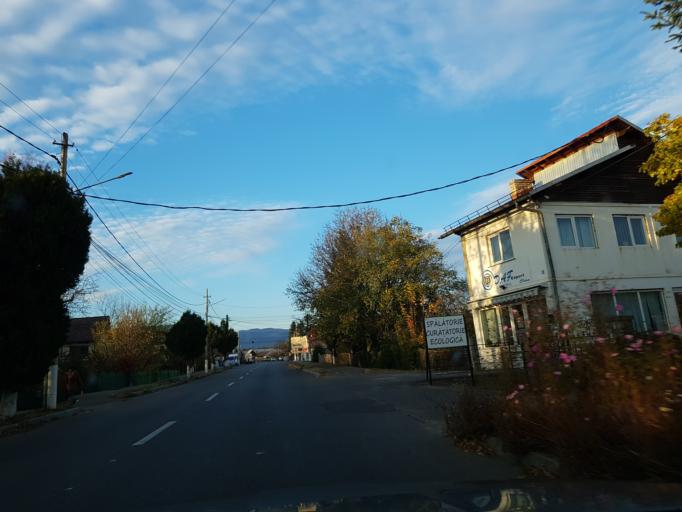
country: RO
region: Prahova
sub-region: Oras Breaza
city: Breaza de Sus
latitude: 45.1938
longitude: 25.6571
